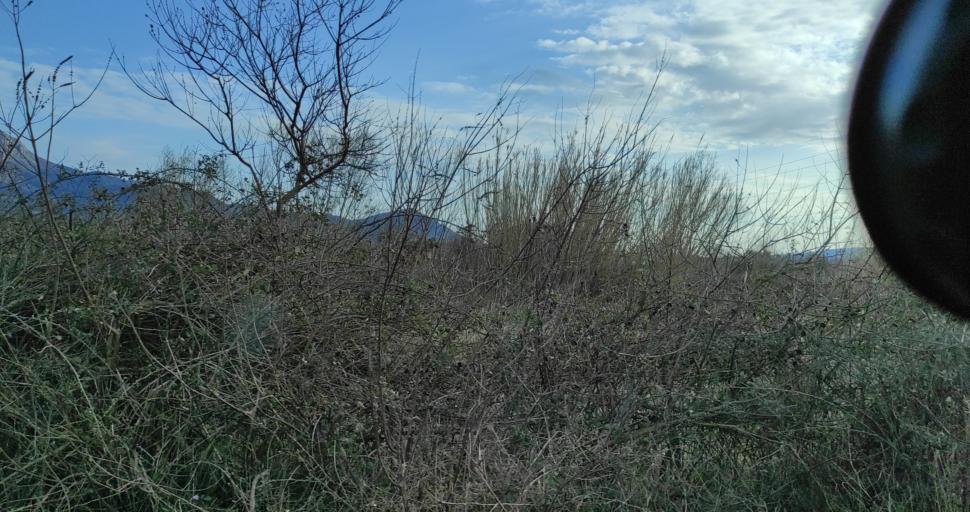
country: AL
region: Lezhe
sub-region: Rrethi i Lezhes
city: Kallmeti i Madh
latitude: 41.8793
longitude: 19.6695
